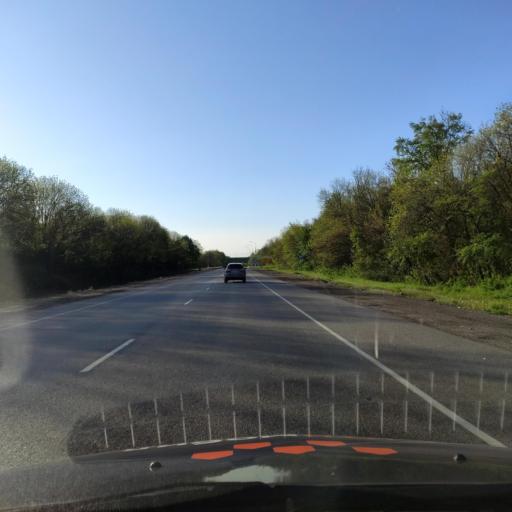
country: RU
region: Lipetsk
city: Yelets
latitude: 52.5506
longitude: 38.7100
